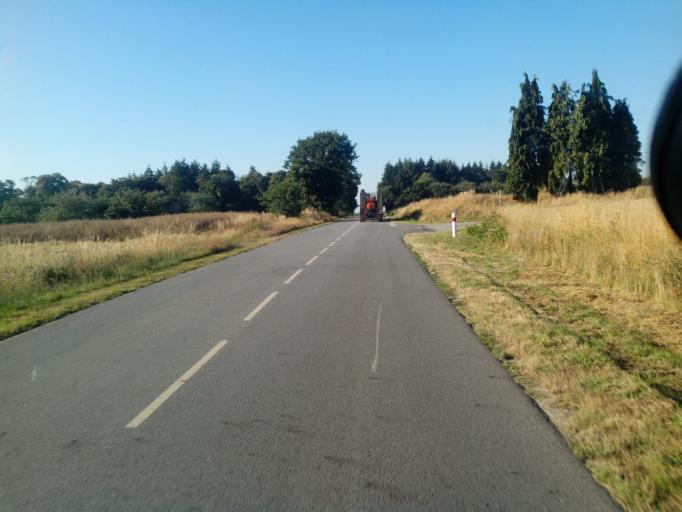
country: FR
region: Brittany
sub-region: Departement du Morbihan
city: Guilliers
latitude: 48.0589
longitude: -2.4123
